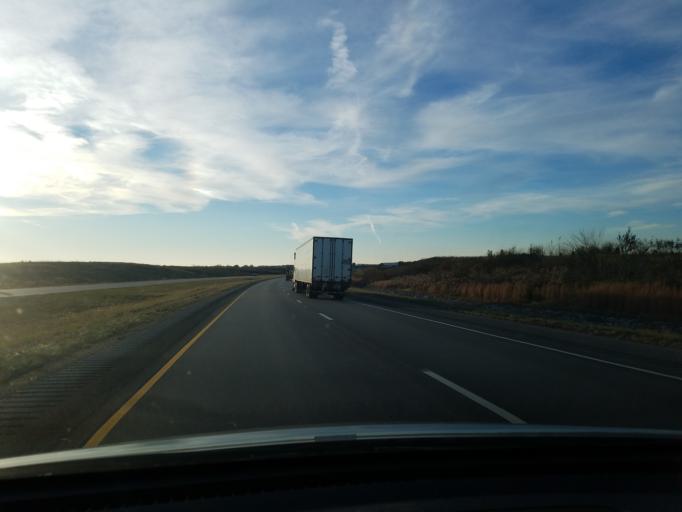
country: US
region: Indiana
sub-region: Spencer County
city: Dale
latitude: 38.1936
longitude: -86.9760
